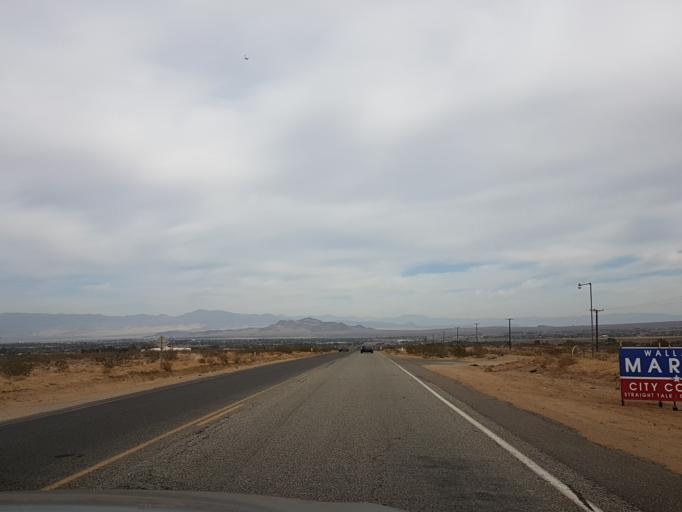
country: US
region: California
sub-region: Kern County
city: Ridgecrest
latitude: 35.5814
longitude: -117.7098
